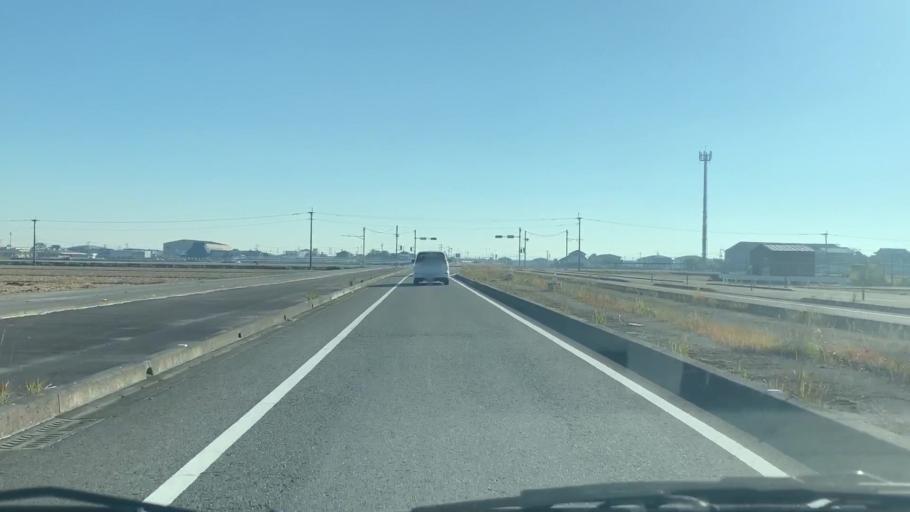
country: JP
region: Saga Prefecture
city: Saga-shi
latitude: 33.2214
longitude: 130.2026
